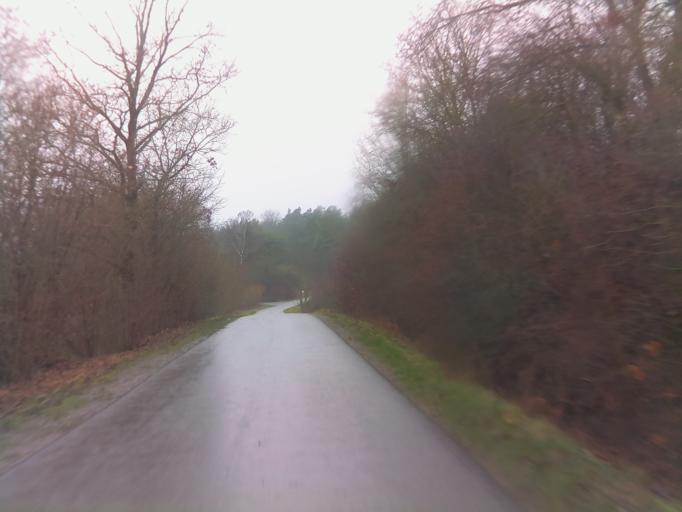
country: DE
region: Thuringia
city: Dingsleben
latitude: 50.4299
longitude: 10.5889
